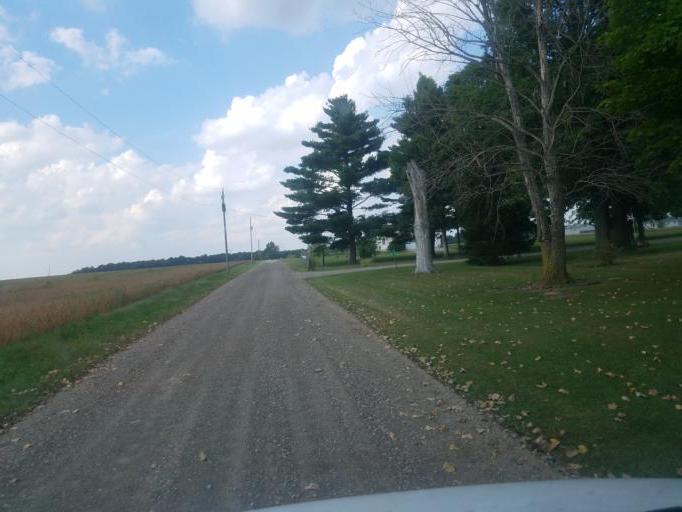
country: US
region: Ohio
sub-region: Hancock County
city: Arlington
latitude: 40.8103
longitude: -83.6898
